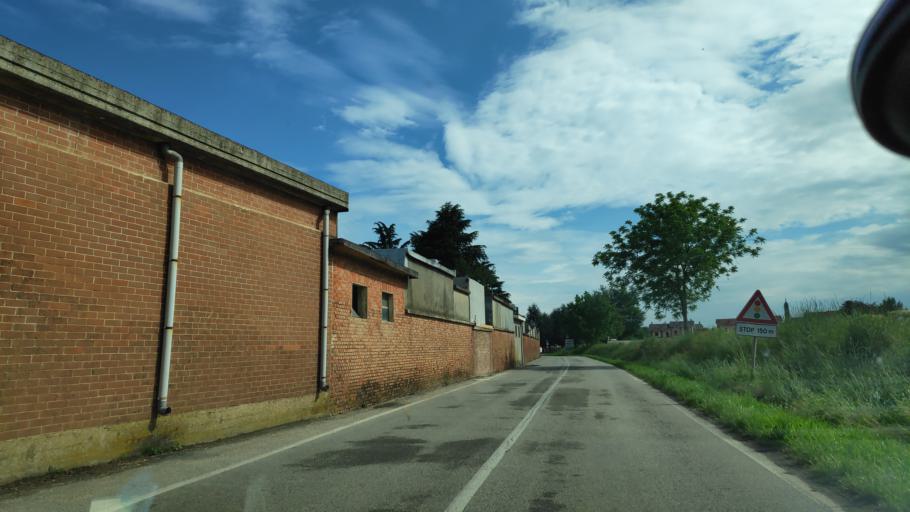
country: IT
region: Piedmont
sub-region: Provincia di Torino
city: Cambiano
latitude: 44.9809
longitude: 7.7820
